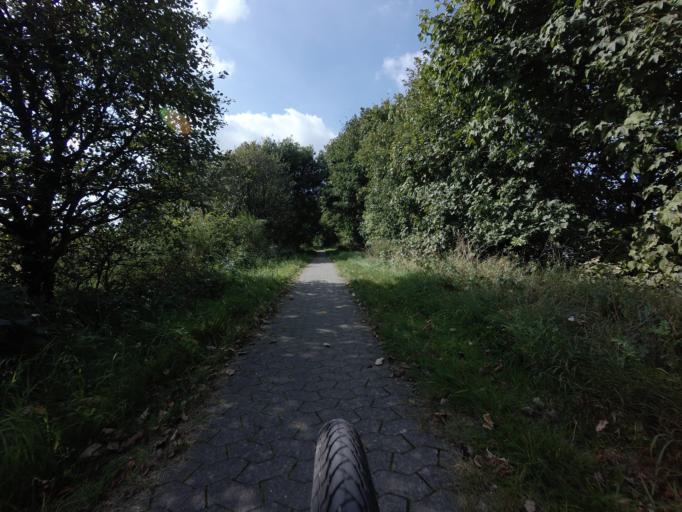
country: DK
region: Central Jutland
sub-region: Viborg Kommune
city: Viborg
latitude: 56.3939
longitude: 9.3110
